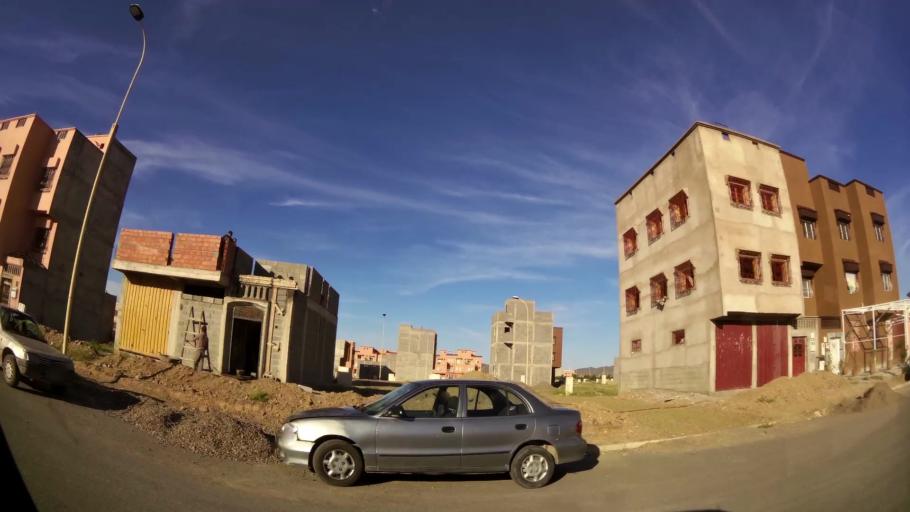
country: MA
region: Marrakech-Tensift-Al Haouz
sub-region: Marrakech
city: Marrakesh
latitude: 31.7583
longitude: -8.1001
